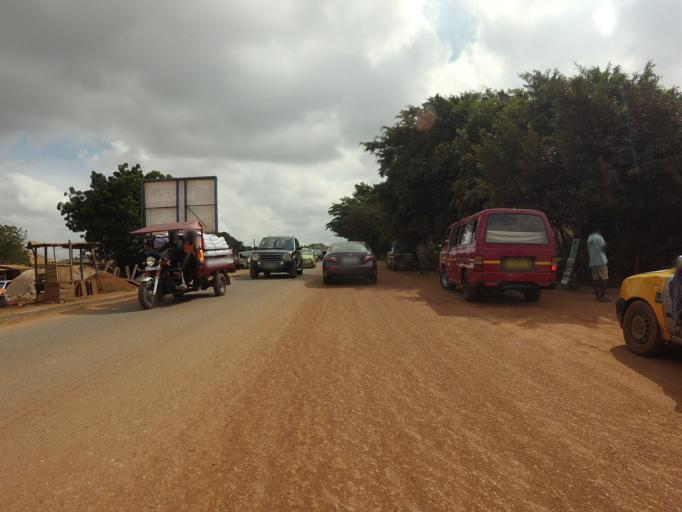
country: GH
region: Greater Accra
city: Teshi Old Town
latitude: 5.6034
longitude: -0.1209
